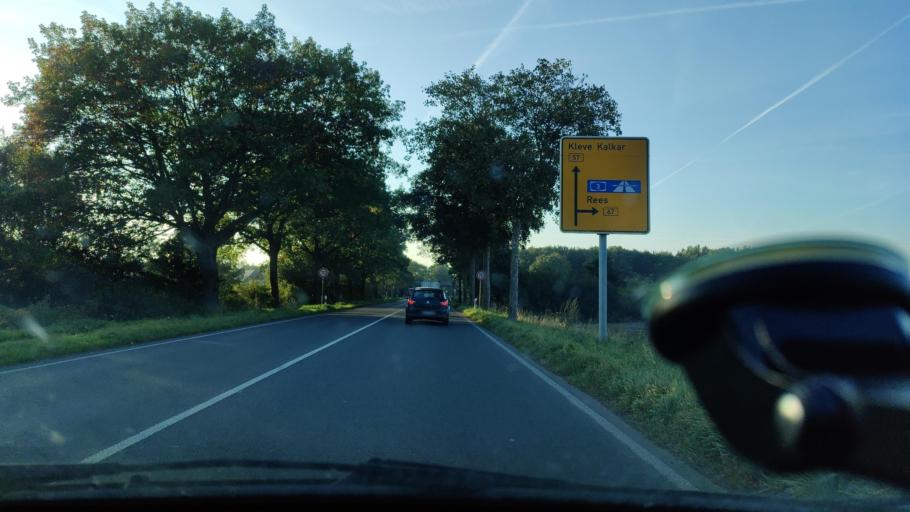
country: DE
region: North Rhine-Westphalia
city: Kalkar
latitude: 51.7113
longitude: 6.3339
